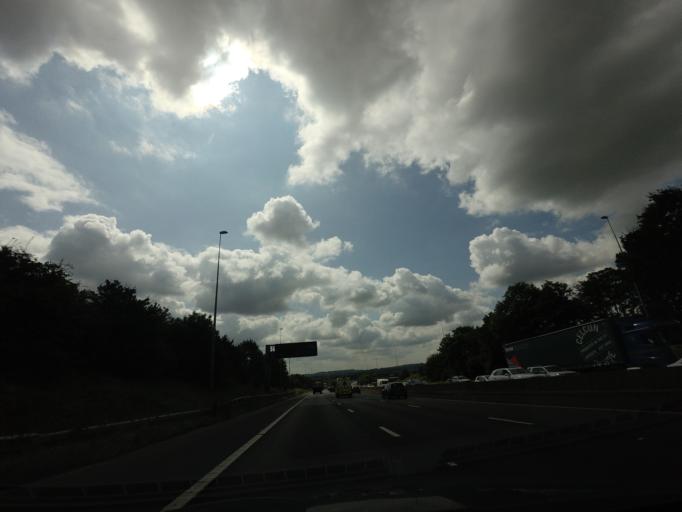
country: GB
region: England
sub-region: Borough of Wigan
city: Shevington
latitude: 53.5806
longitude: -2.6940
